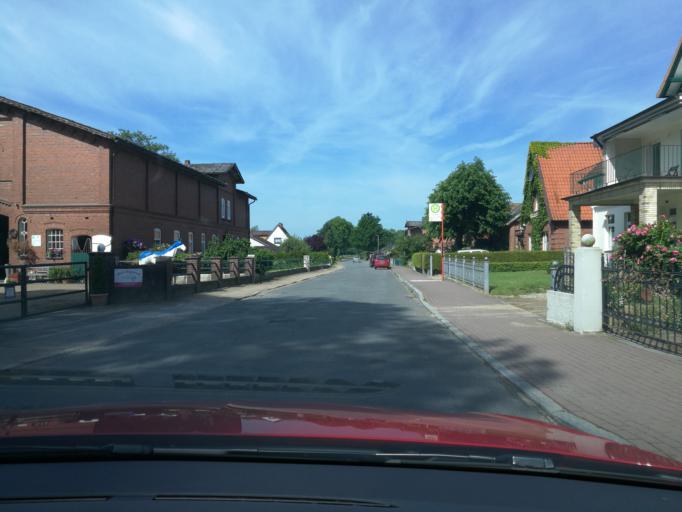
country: DE
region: Schleswig-Holstein
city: Lasbek
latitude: 53.7329
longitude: 10.3598
